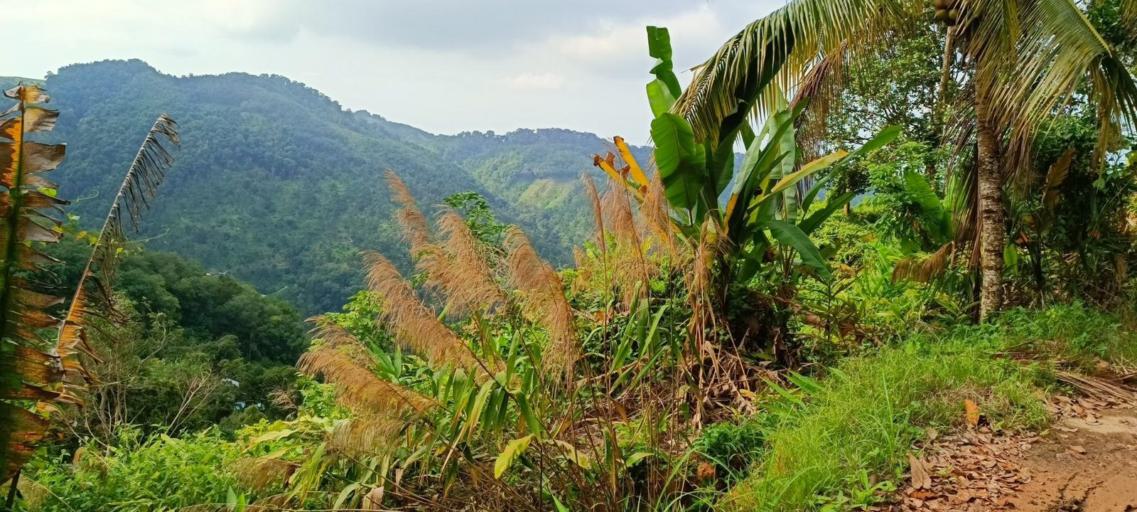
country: MY
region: Penang
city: Kampung Sungai Ara
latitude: 5.3781
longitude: 100.2449
